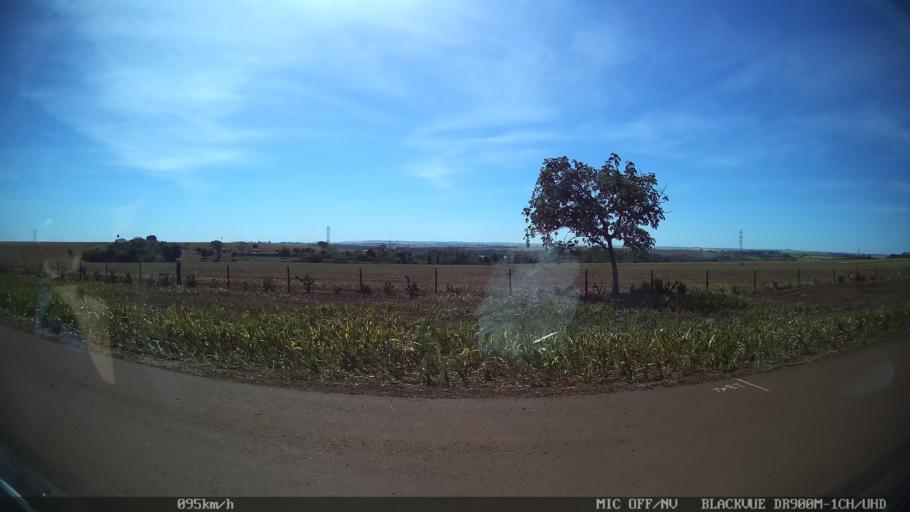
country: BR
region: Sao Paulo
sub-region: Sao Joaquim Da Barra
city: Sao Joaquim da Barra
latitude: -20.5210
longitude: -47.8626
